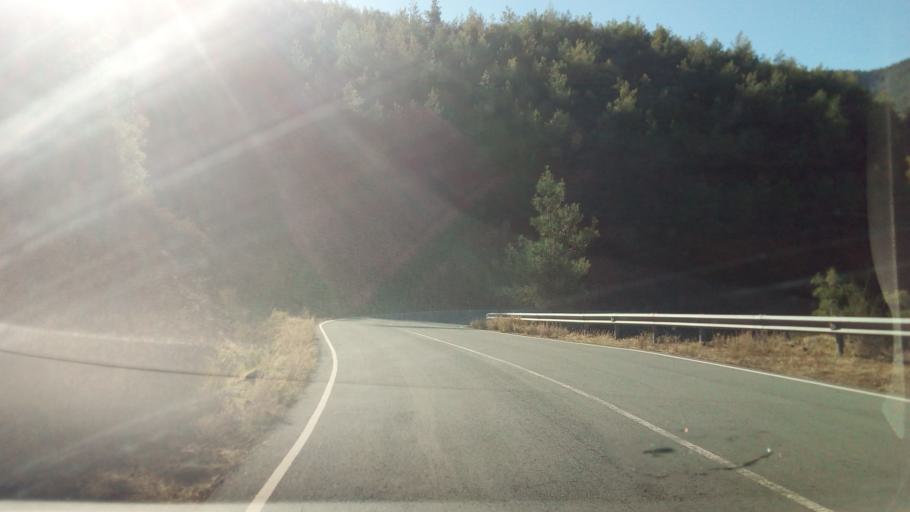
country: CY
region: Lefkosia
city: Kato Pyrgos
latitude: 35.1060
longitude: 32.7478
